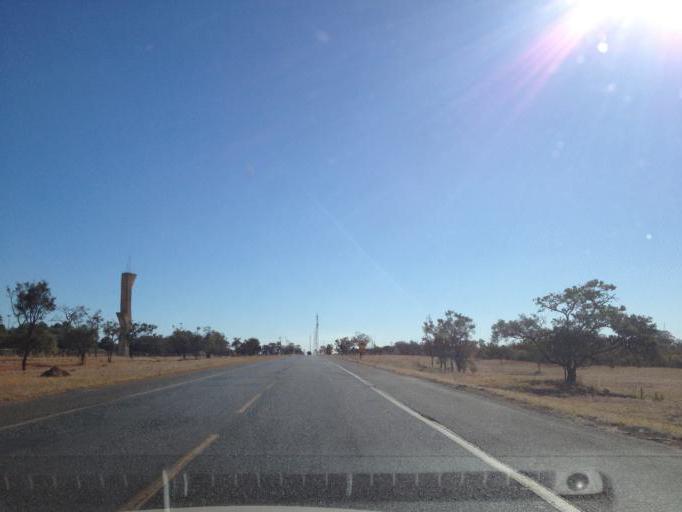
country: BR
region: Federal District
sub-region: Brasilia
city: Brasilia
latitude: -15.6929
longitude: -47.8395
